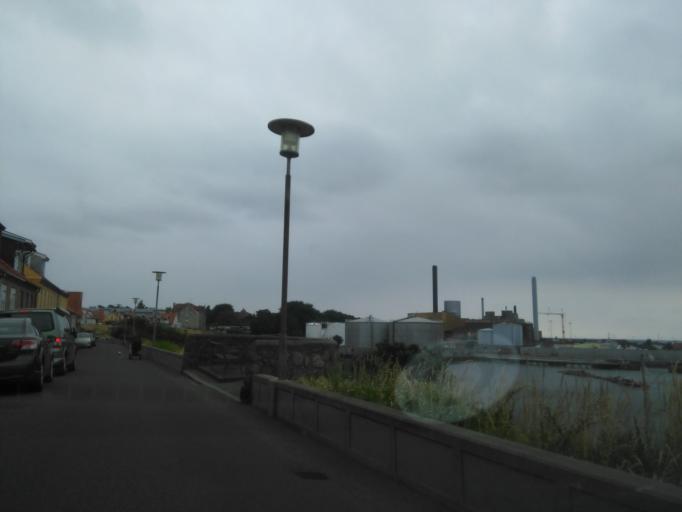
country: DK
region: Capital Region
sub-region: Bornholm Kommune
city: Ronne
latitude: 55.0977
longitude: 14.6983
